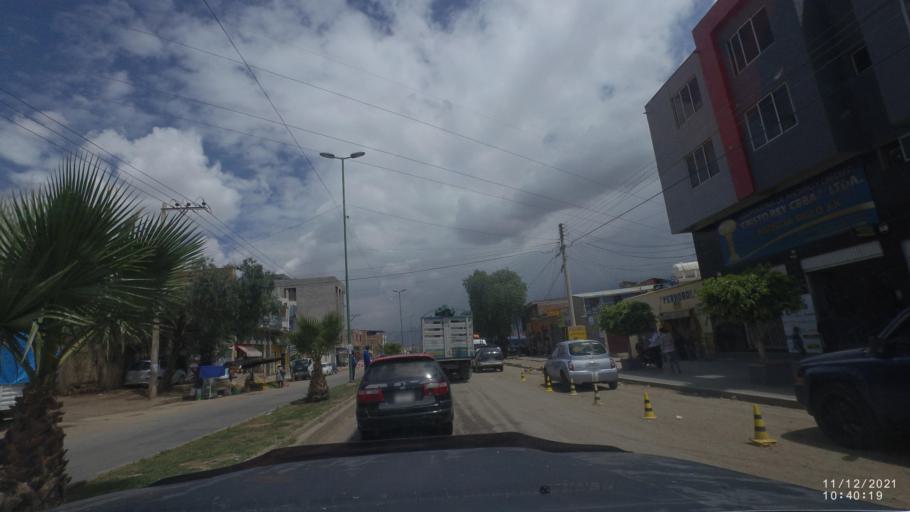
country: BO
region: Cochabamba
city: Cochabamba
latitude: -17.4326
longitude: -66.1270
